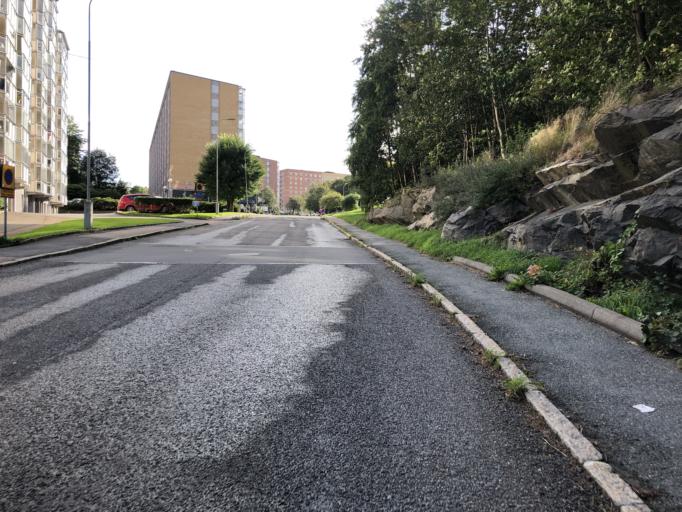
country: SE
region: Vaestra Goetaland
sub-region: Goteborg
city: Majorna
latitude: 57.7283
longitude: 11.8987
